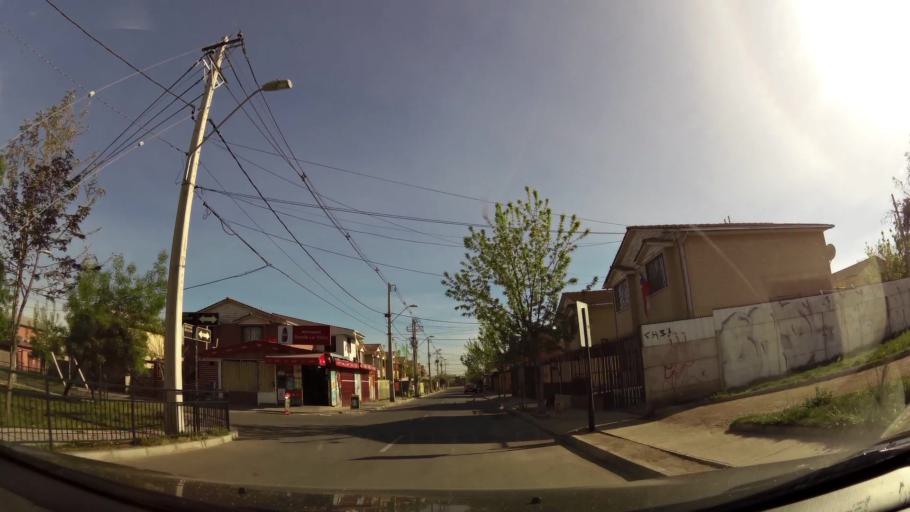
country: CL
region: Santiago Metropolitan
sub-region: Provincia de Cordillera
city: Puente Alto
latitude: -33.6140
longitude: -70.5947
